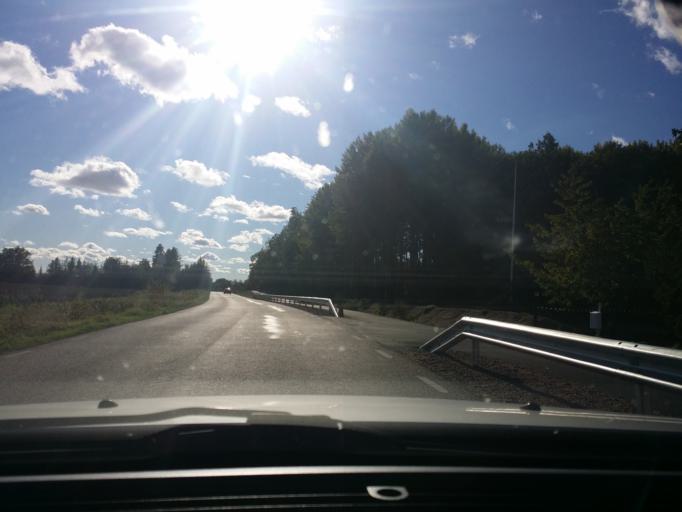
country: SE
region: Vaestmanland
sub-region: Vasteras
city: Vasteras
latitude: 59.5677
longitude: 16.4832
